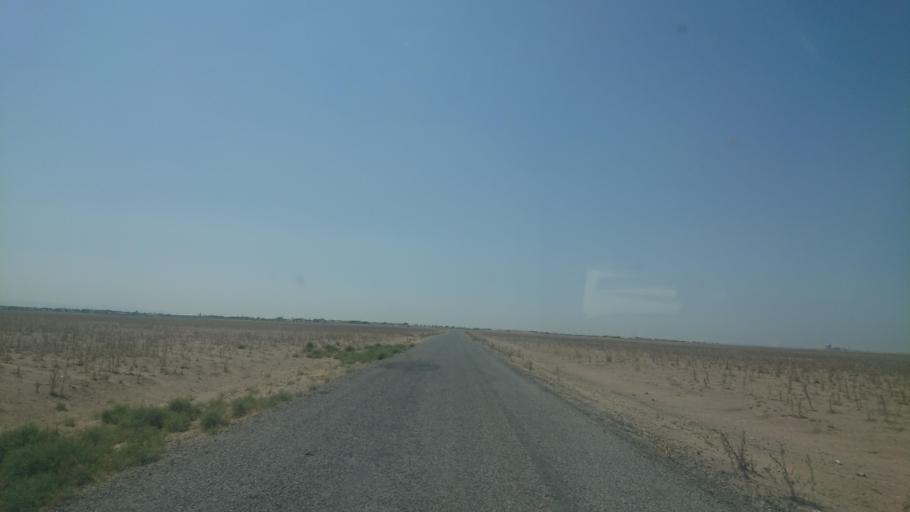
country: TR
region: Aksaray
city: Yesilova
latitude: 38.3072
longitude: 33.7351
